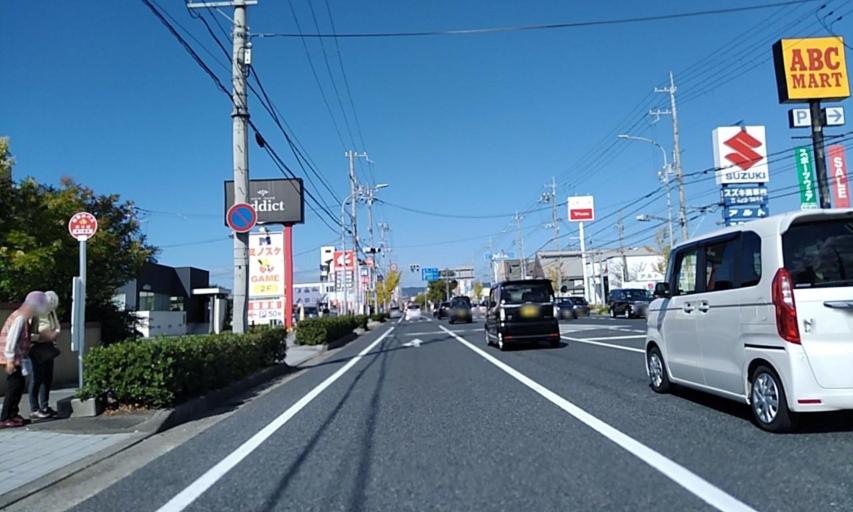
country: JP
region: Wakayama
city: Wakayama-shi
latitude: 34.2014
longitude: 135.1849
